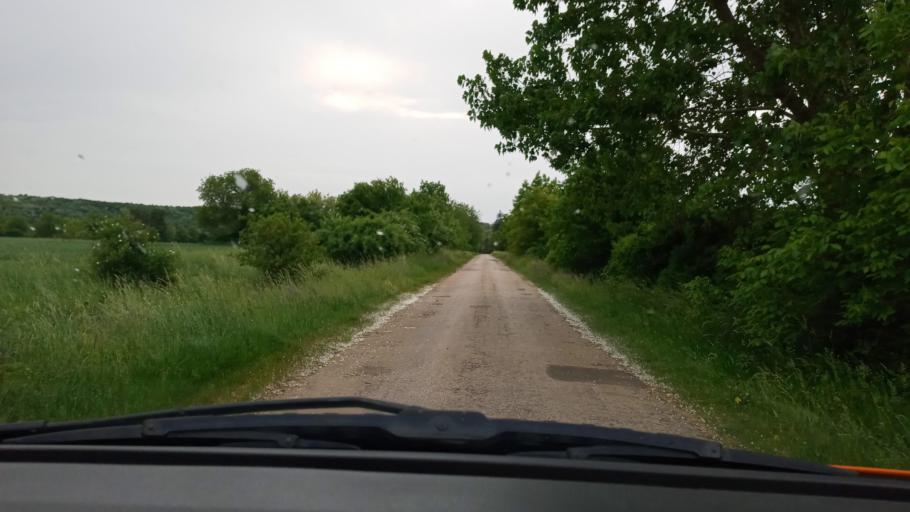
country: HU
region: Baranya
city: Harkany
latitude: 45.9036
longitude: 18.1378
